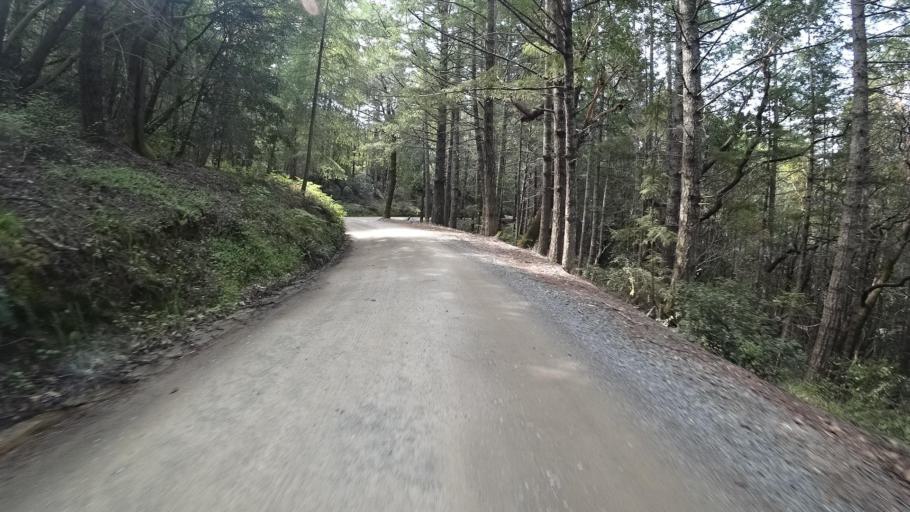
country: US
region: California
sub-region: Humboldt County
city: Redway
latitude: 40.0287
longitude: -123.8417
